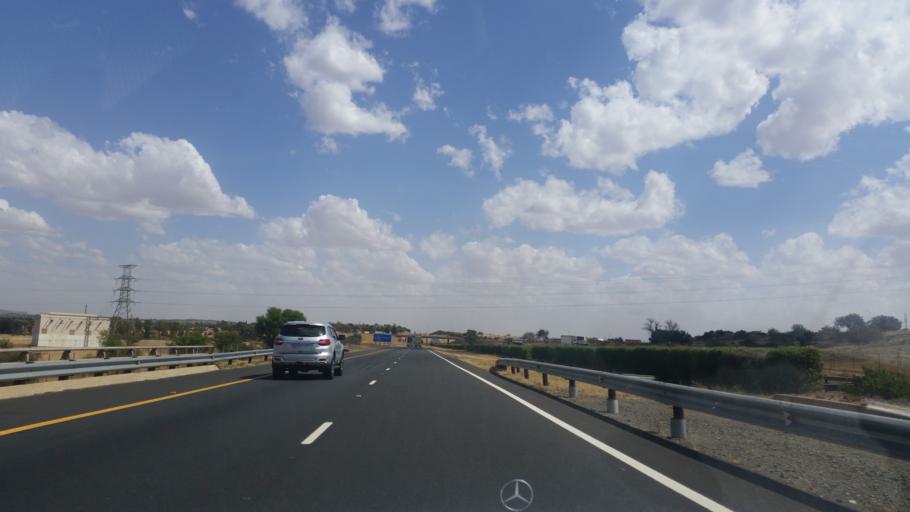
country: ZA
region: Orange Free State
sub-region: Mangaung Metropolitan Municipality
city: Bloemfontein
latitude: -29.0844
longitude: 26.1754
